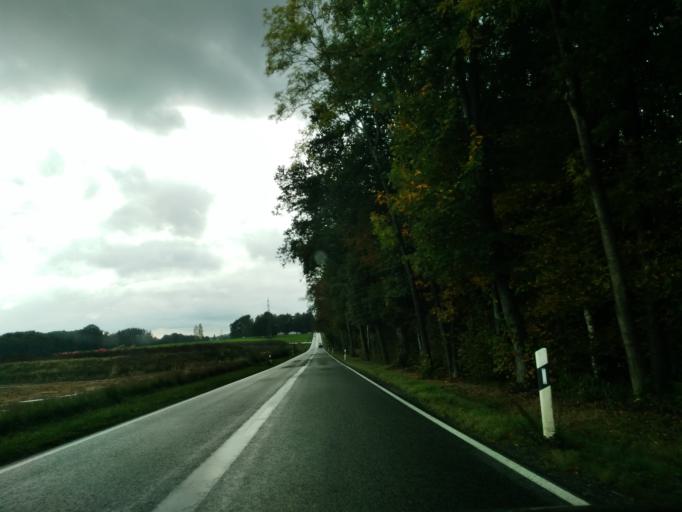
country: DE
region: Rheinland-Pfalz
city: Windhagen
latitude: 50.6676
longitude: 7.3618
